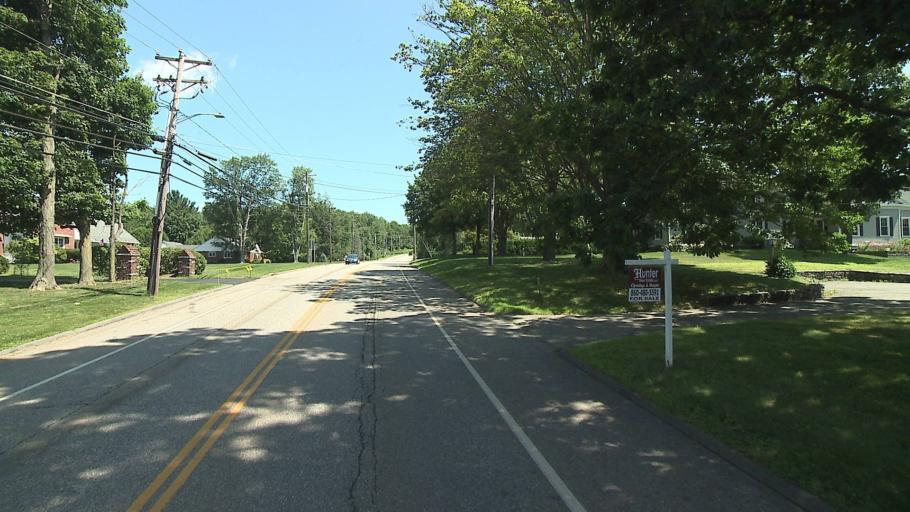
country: US
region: Connecticut
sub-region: Litchfield County
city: Torrington
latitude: 41.8063
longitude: -73.0994
